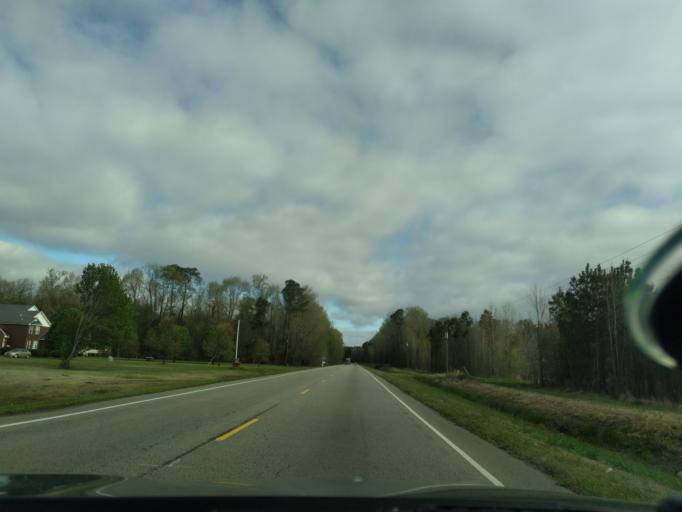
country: US
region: North Carolina
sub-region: Washington County
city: Plymouth
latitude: 35.8761
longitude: -76.6947
